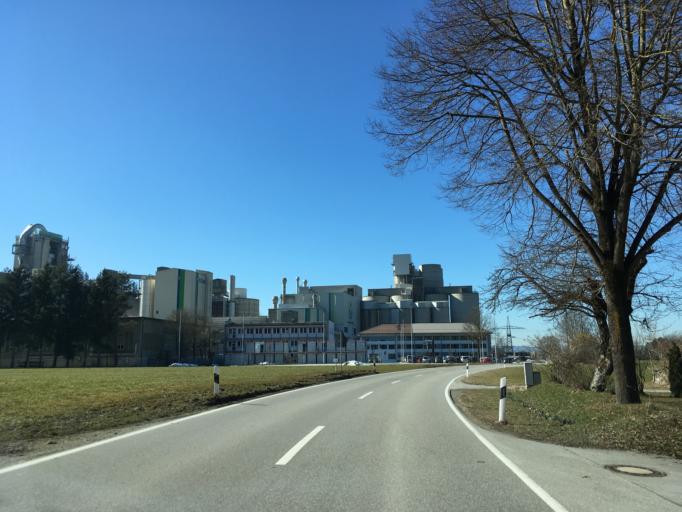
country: DE
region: Bavaria
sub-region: Upper Bavaria
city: Rohrdorf
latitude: 47.7930
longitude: 12.1858
